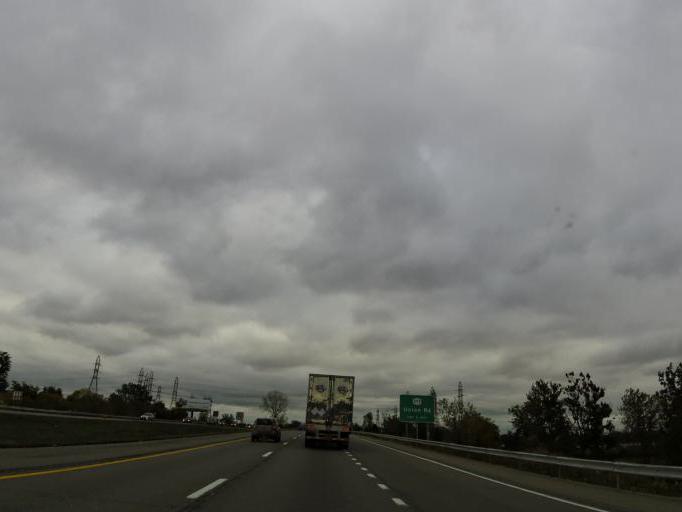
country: US
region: New York
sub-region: Erie County
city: West Seneca
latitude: 42.8463
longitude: -78.7774
